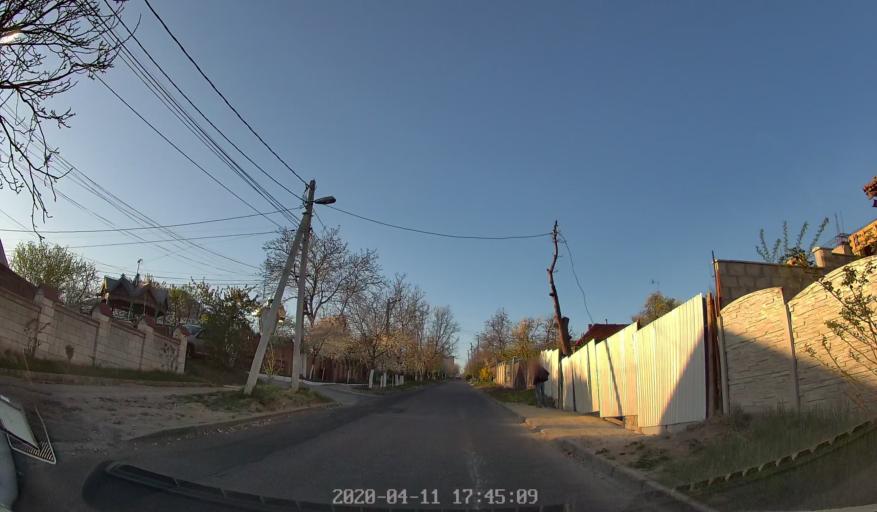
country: MD
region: Chisinau
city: Chisinau
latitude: 46.9827
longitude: 28.8229
